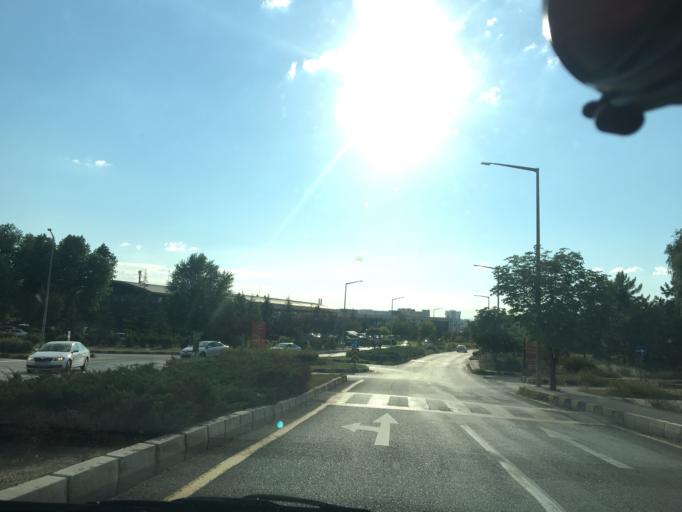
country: TR
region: Ankara
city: Ankara
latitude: 39.8997
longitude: 32.7773
